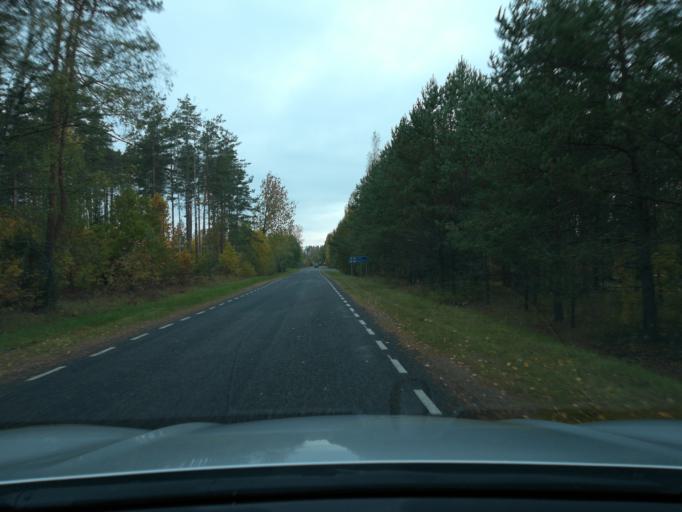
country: EE
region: Ida-Virumaa
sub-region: Johvi vald
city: Johvi
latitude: 59.0146
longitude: 27.4170
